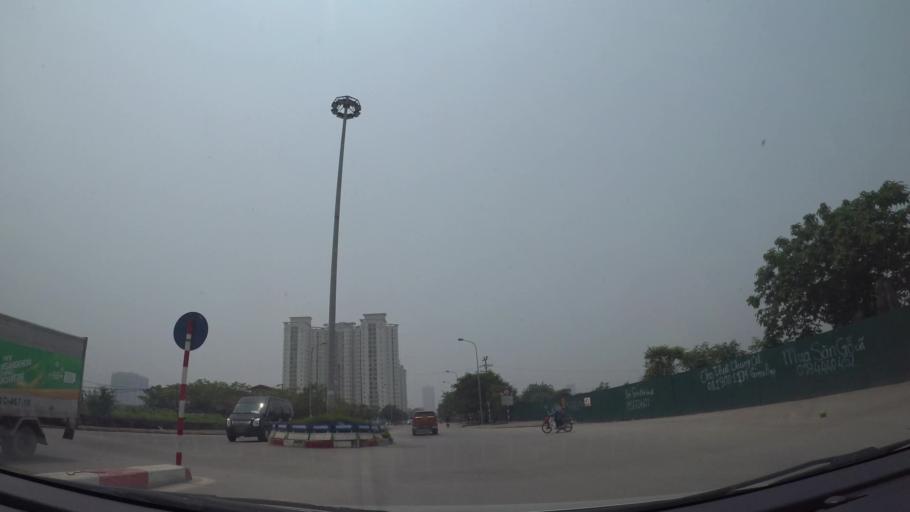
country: VN
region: Ha Noi
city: Thanh Xuan
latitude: 20.9982
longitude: 105.7803
